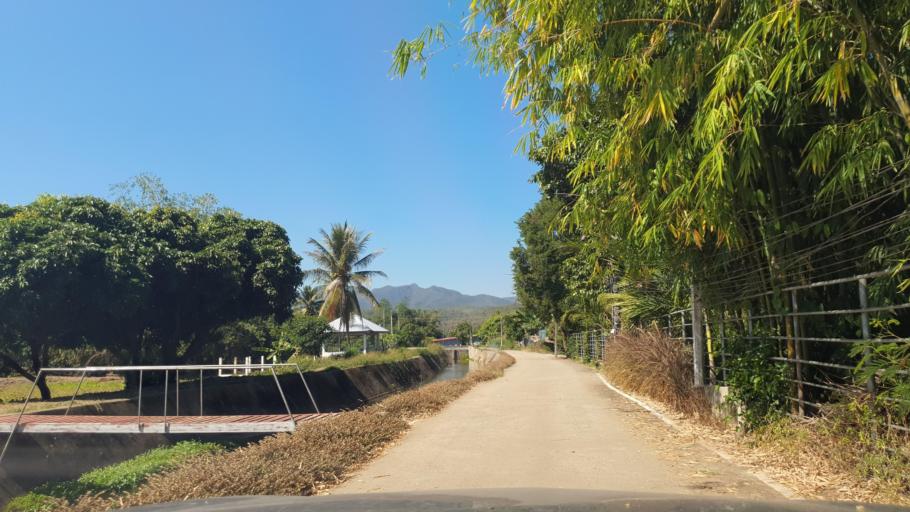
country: TH
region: Chiang Mai
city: Mae Wang
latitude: 18.6774
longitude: 98.8194
